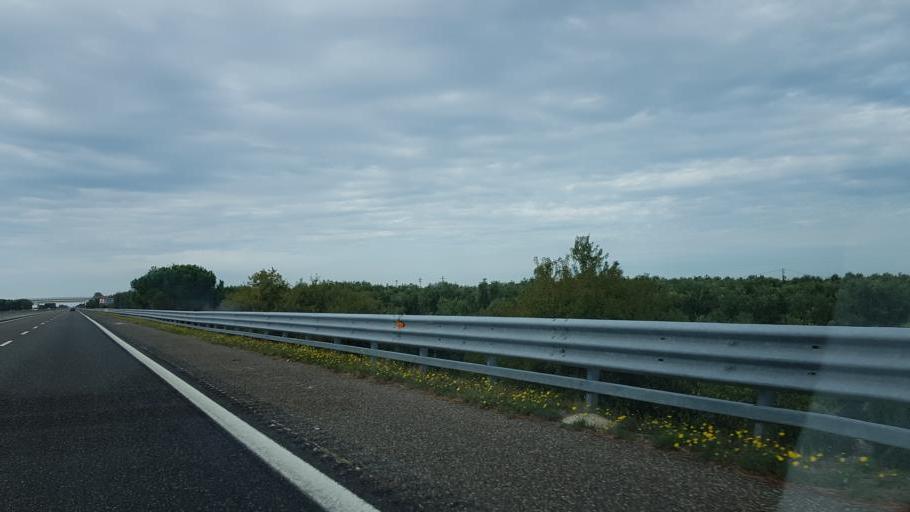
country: IT
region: Apulia
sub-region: Provincia di Barletta - Andria - Trani
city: Bisceglie
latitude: 41.1860
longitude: 16.5213
